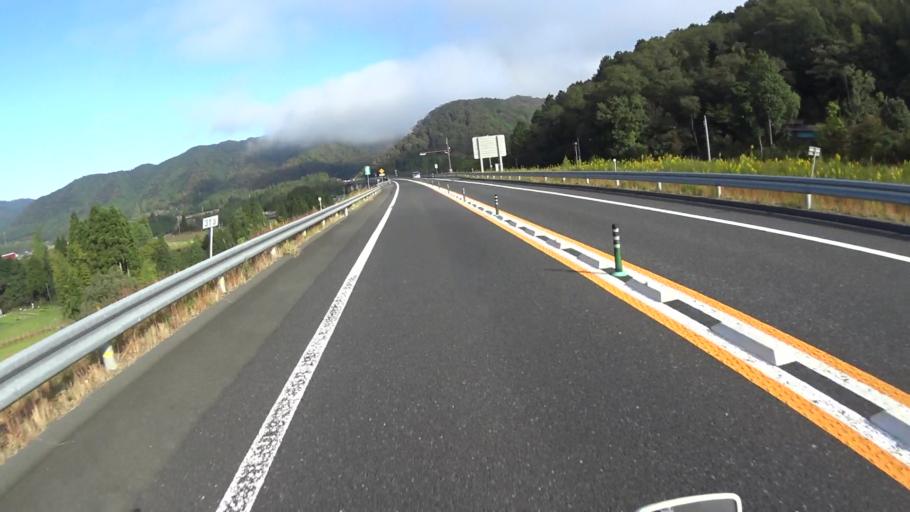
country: JP
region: Kyoto
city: Ayabe
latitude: 35.2917
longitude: 135.3356
